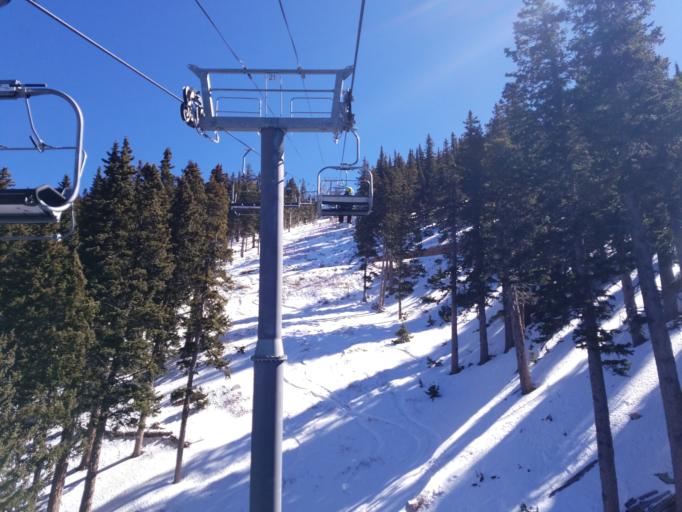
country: US
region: New Mexico
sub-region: Santa Fe County
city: Santa Fe
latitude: 35.7923
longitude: -105.7798
